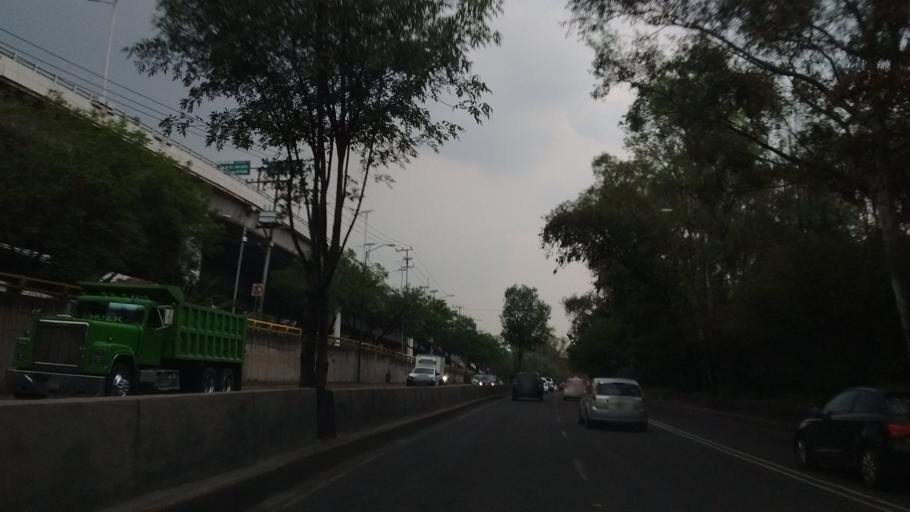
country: MX
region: Mexico City
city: Polanco
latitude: 19.4149
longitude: -99.1930
